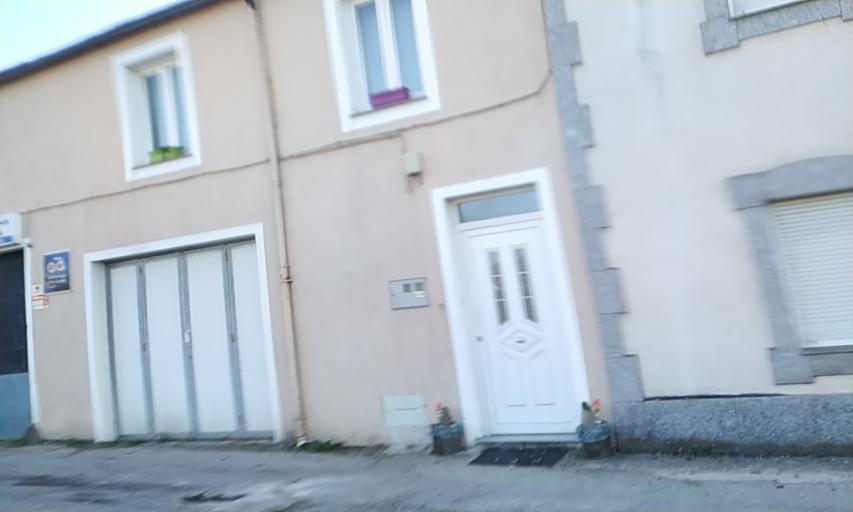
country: ES
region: Galicia
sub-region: Provincia de Lugo
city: Corgo
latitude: 42.9570
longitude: -7.4702
